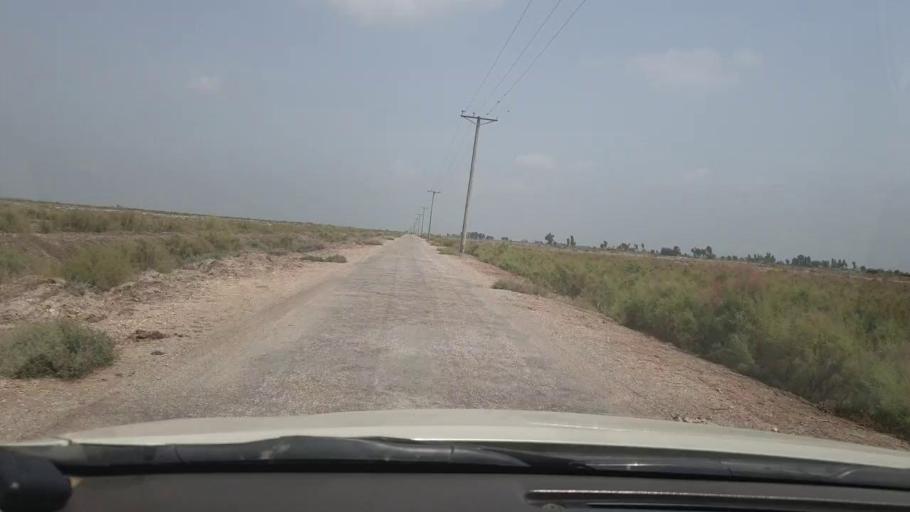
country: PK
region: Sindh
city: Garhi Yasin
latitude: 27.9911
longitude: 68.5014
